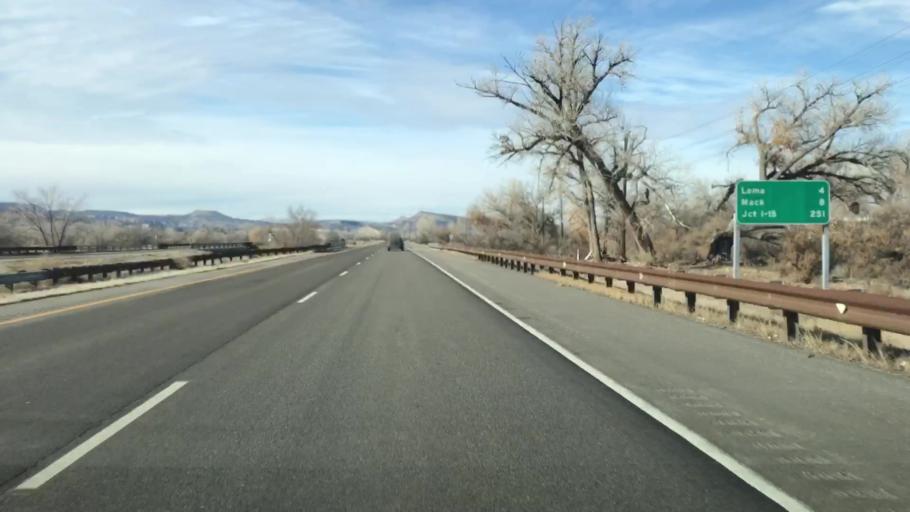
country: US
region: Colorado
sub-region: Mesa County
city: Fruita
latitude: 39.1589
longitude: -108.7521
